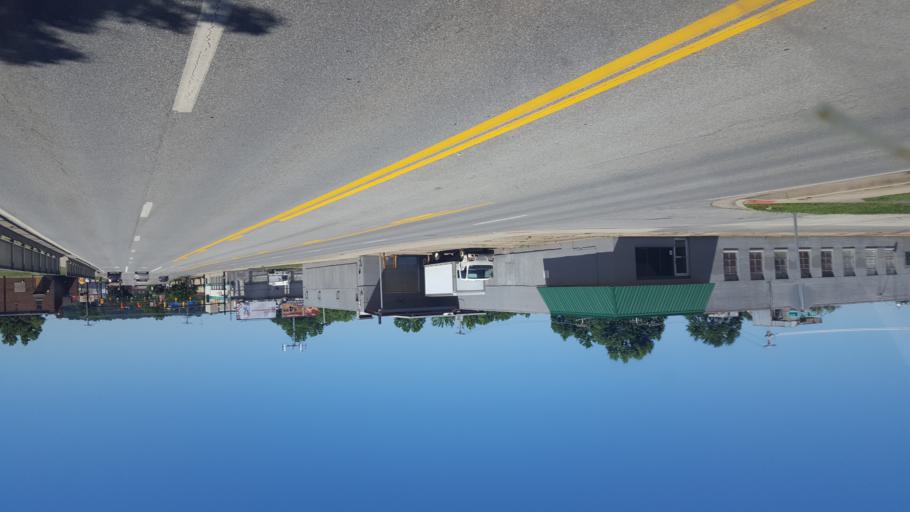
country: US
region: West Virginia
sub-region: Cabell County
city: Huntington
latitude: 38.4129
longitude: -82.4290
